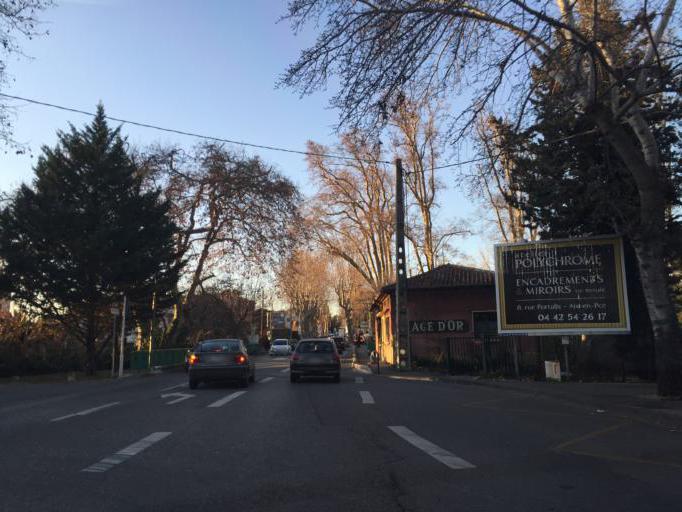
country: FR
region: Provence-Alpes-Cote d'Azur
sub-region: Departement des Bouches-du-Rhone
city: Aix-en-Provence
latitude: 43.5180
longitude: 5.4642
